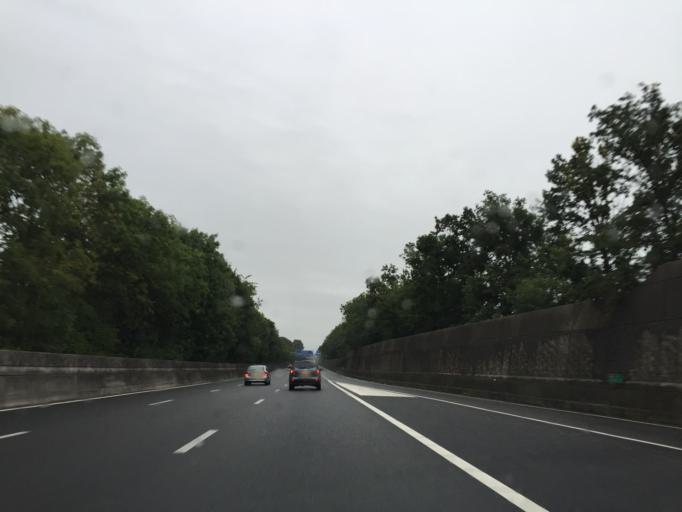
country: NL
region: Limburg
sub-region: Gemeente Meerssen
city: Meerssen
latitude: 50.8913
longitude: 5.7440
